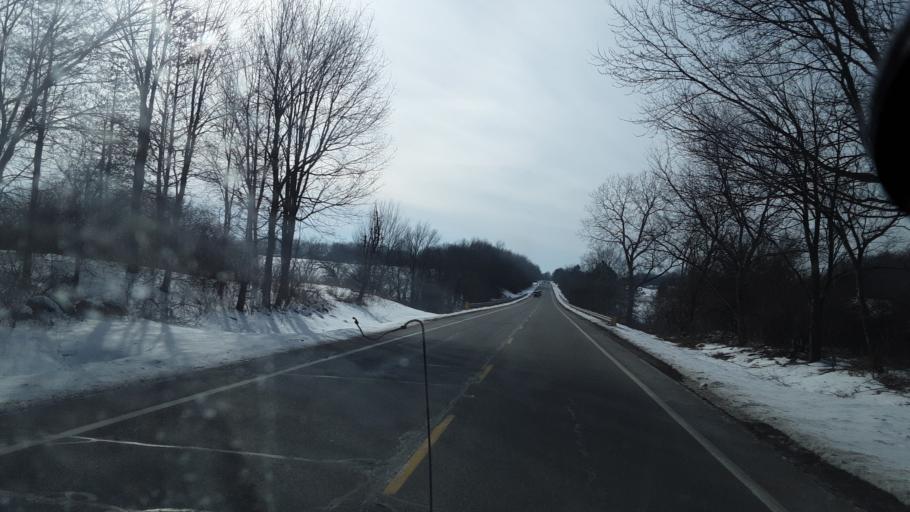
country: US
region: Ohio
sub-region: Stark County
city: Hartville
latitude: 41.0298
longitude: -81.3121
